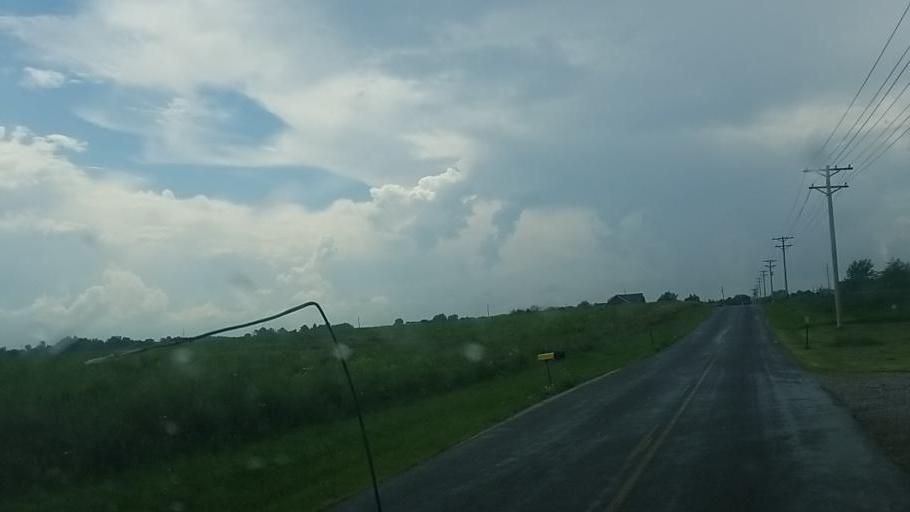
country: US
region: Ohio
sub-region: Lorain County
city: Grafton
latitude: 41.1581
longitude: -82.0129
